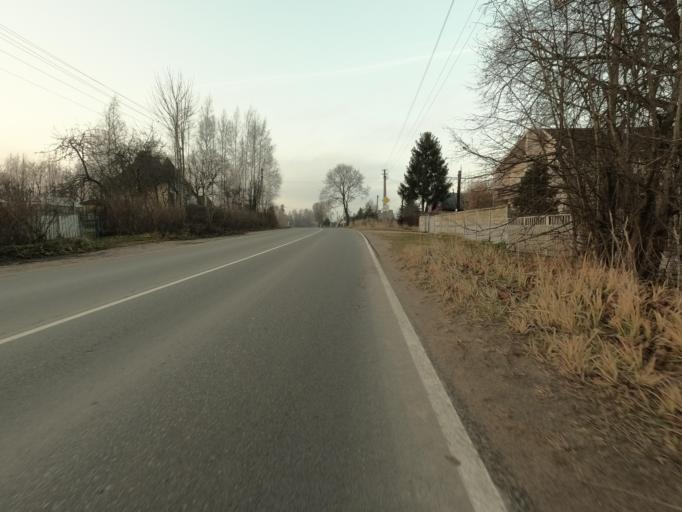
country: RU
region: Leningrad
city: Kirovsk
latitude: 59.8303
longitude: 30.9875
